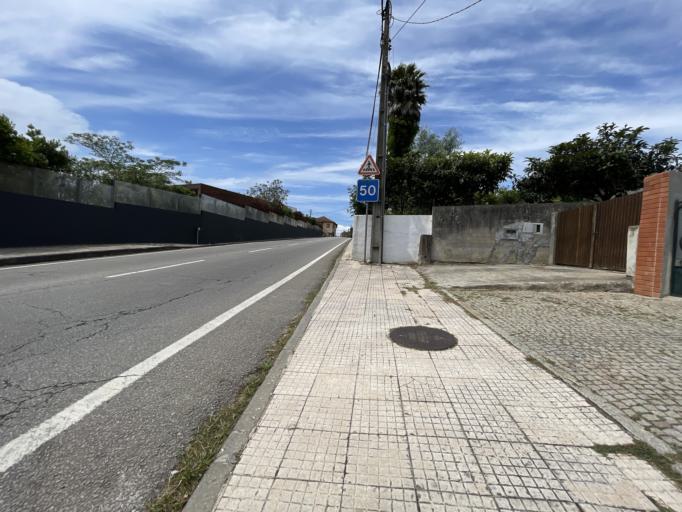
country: PT
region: Aveiro
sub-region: Ovar
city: Cortegaca
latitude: 40.9411
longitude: -8.6187
